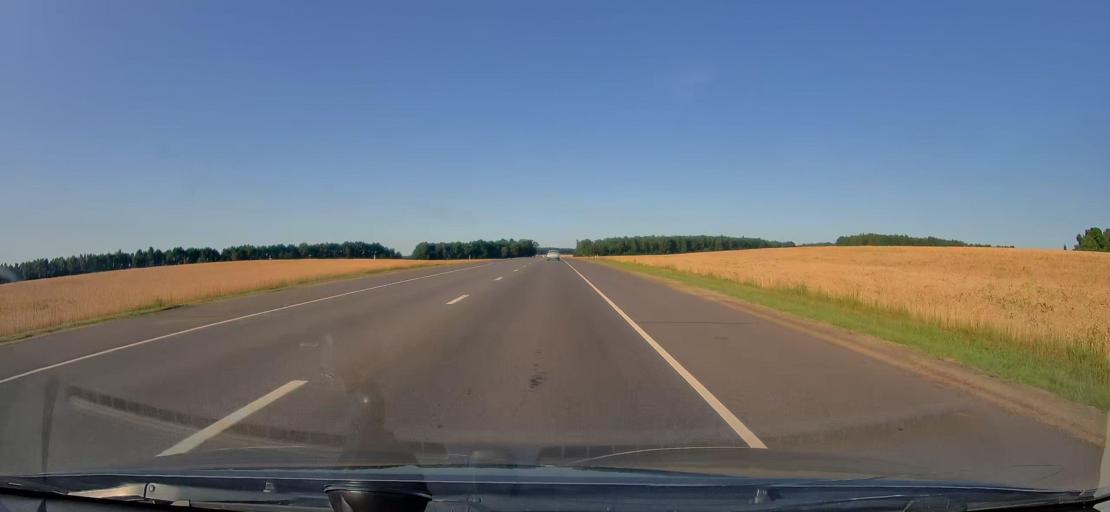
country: RU
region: Orjol
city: Spasskoye-Lutovinovo
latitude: 53.3095
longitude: 36.6868
